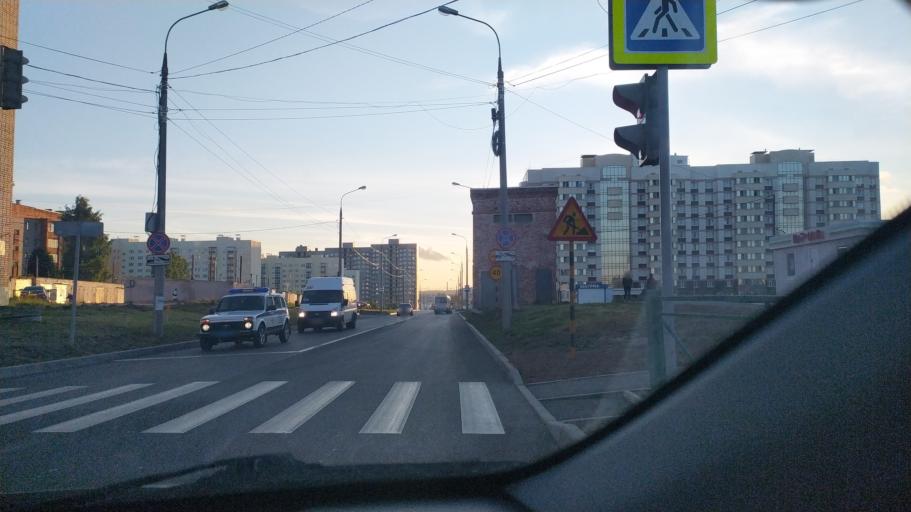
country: RU
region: Chuvashia
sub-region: Cheboksarskiy Rayon
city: Cheboksary
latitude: 56.1156
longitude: 47.2221
